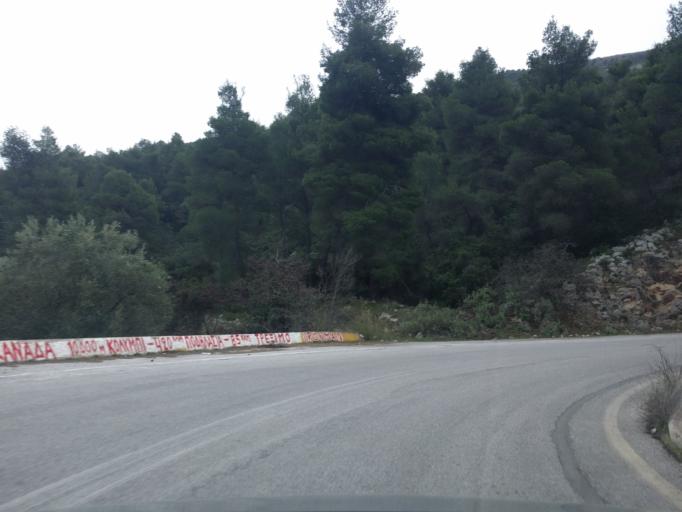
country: GR
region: Attica
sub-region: Nomarchia Dytikis Attikis
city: Vilia
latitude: 38.1424
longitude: 23.2572
